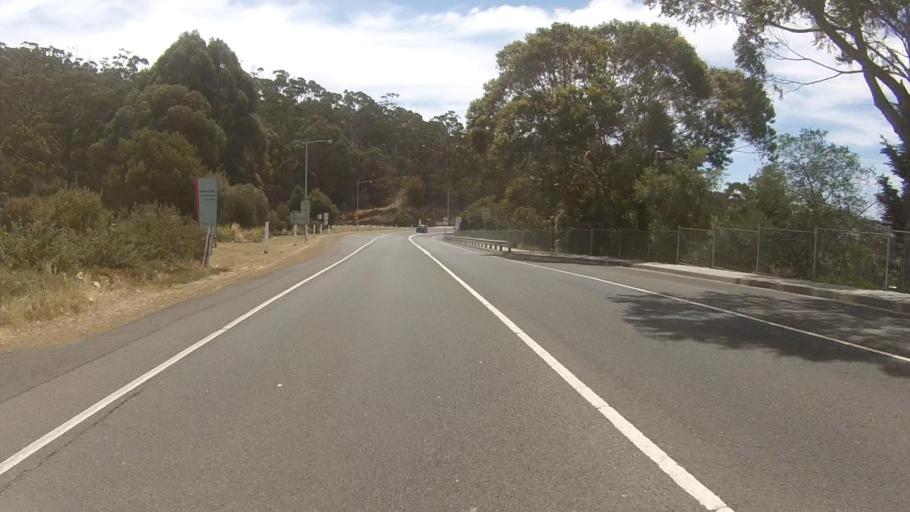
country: AU
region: Tasmania
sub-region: Kingborough
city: Taroona
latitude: -42.9318
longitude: 147.3568
